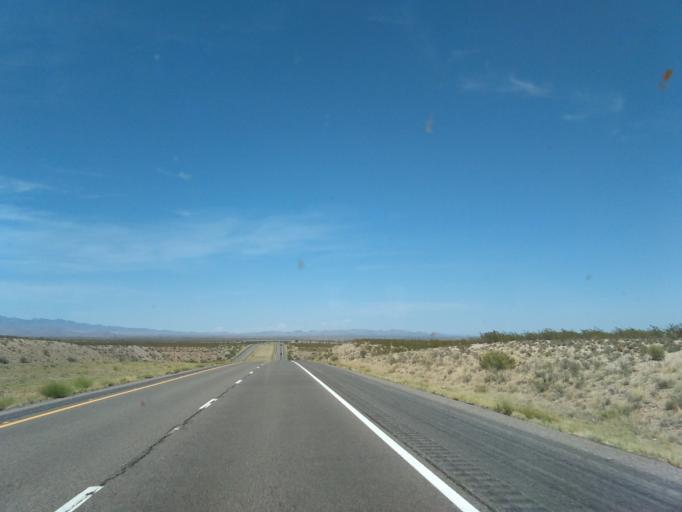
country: US
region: New Mexico
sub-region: Sierra County
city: Elephant Butte
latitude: 33.5851
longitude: -107.1638
